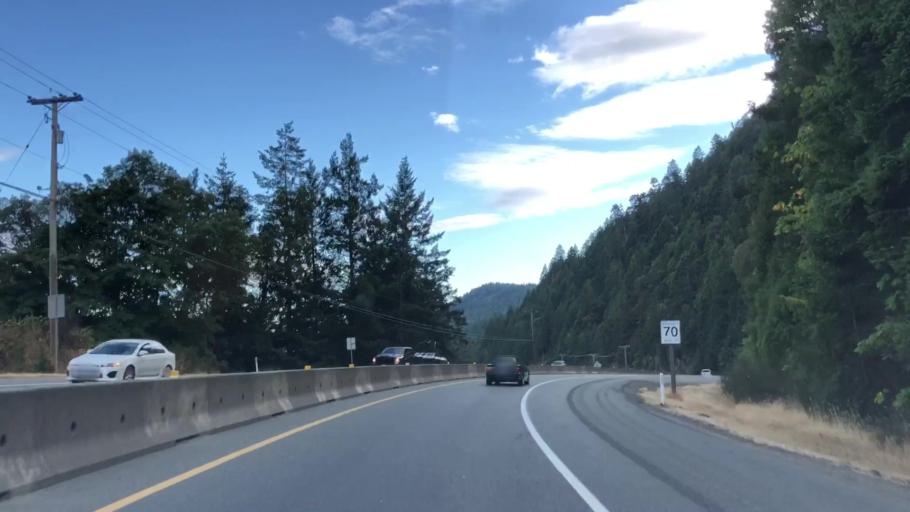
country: CA
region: British Columbia
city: Langford
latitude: 48.5037
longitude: -123.5551
